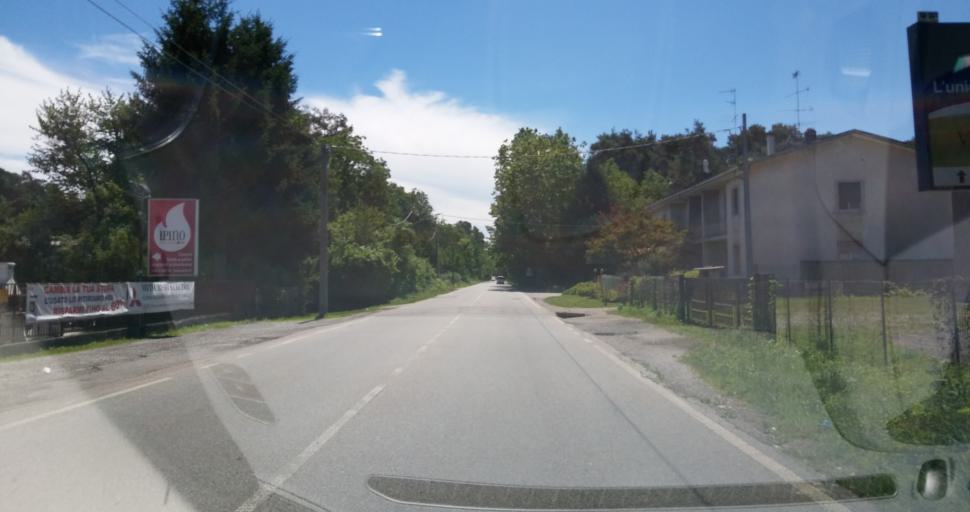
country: IT
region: Lombardy
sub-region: Provincia di Varese
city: Vergiate
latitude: 45.7107
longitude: 8.6954
